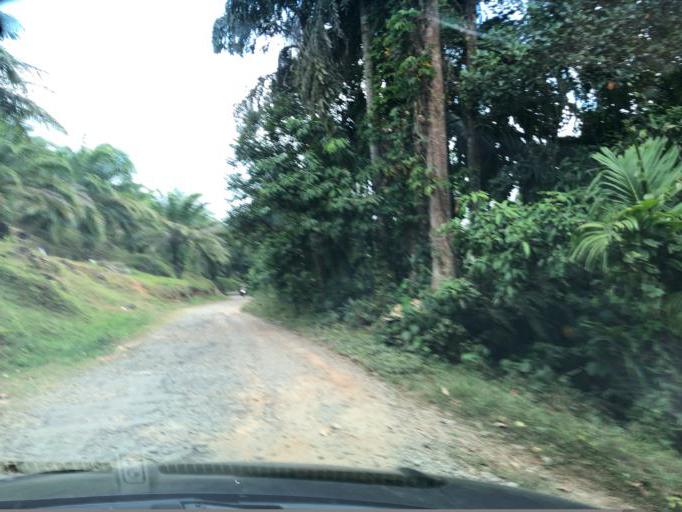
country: LK
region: Western
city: Horawala Junction
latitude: 6.5466
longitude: 80.0940
